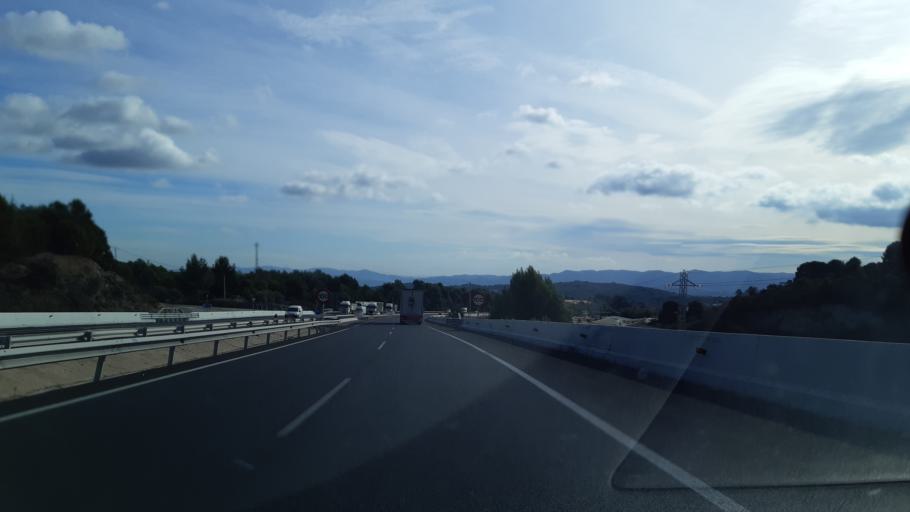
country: ES
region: Catalonia
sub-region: Provincia de Barcelona
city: Collbato
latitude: 41.5843
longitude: 1.7744
